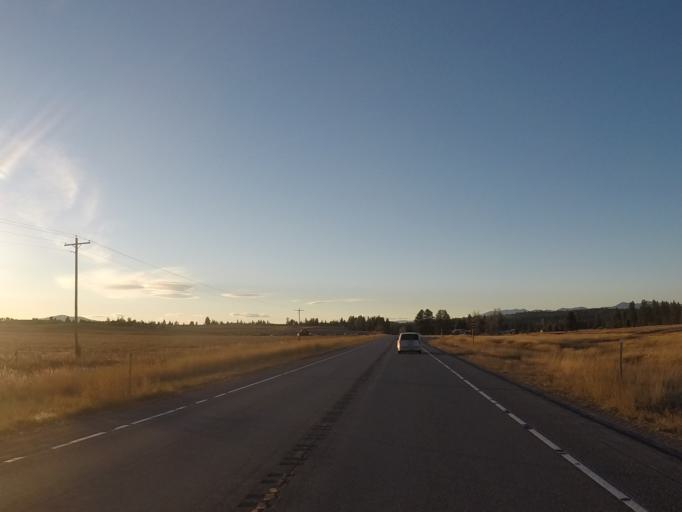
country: US
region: Montana
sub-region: Lewis and Clark County
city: Lincoln
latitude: 46.9939
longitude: -113.0218
